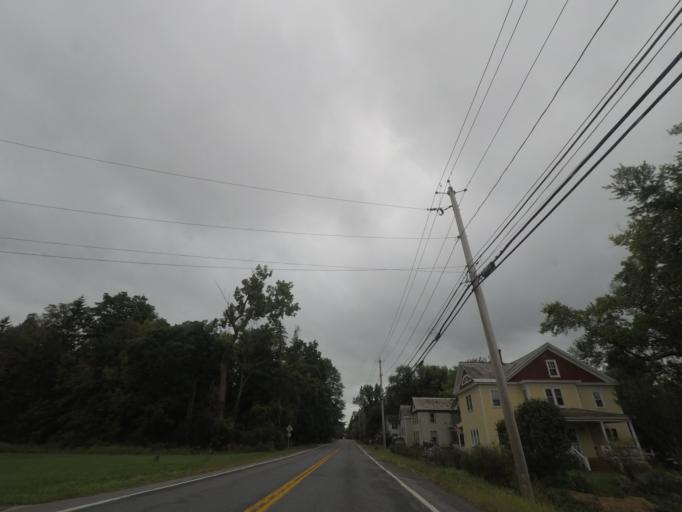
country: US
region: New York
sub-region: Rensselaer County
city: Hoosick Falls
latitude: 42.9242
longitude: -73.3477
